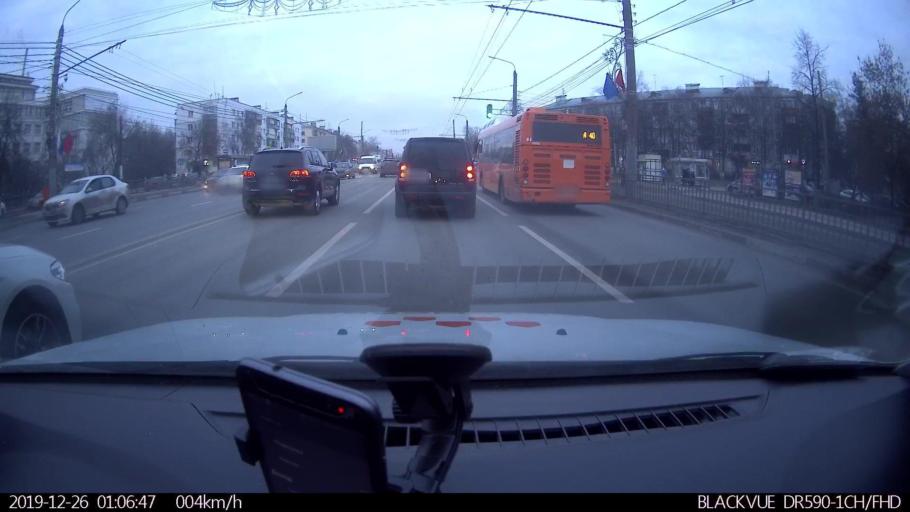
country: RU
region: Nizjnij Novgorod
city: Nizhniy Novgorod
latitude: 56.2894
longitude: 43.9312
